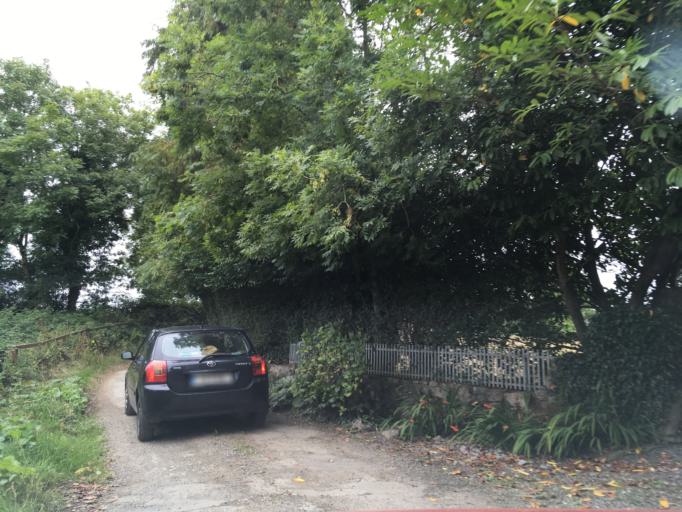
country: IE
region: Munster
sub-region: An Clar
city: Ennis
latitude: 52.7255
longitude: -9.0933
